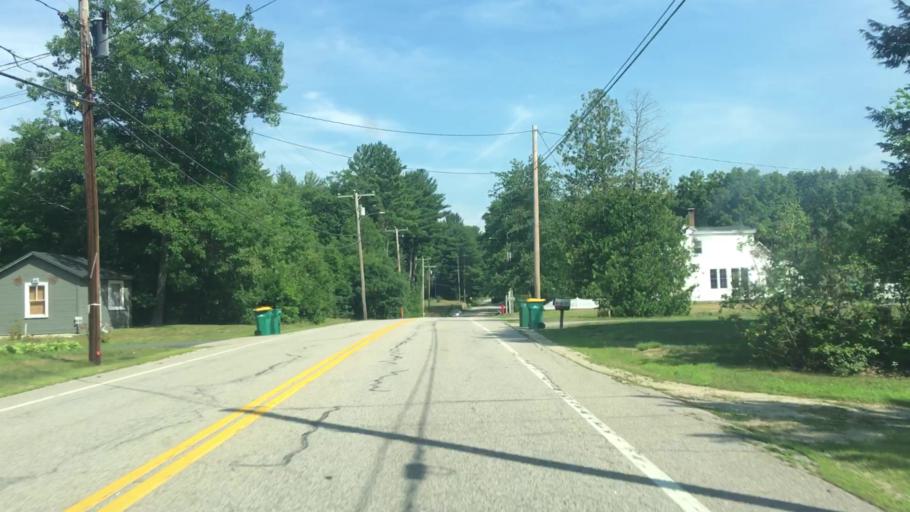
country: US
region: New Hampshire
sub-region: Strafford County
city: Rochester
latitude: 43.2756
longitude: -70.9605
